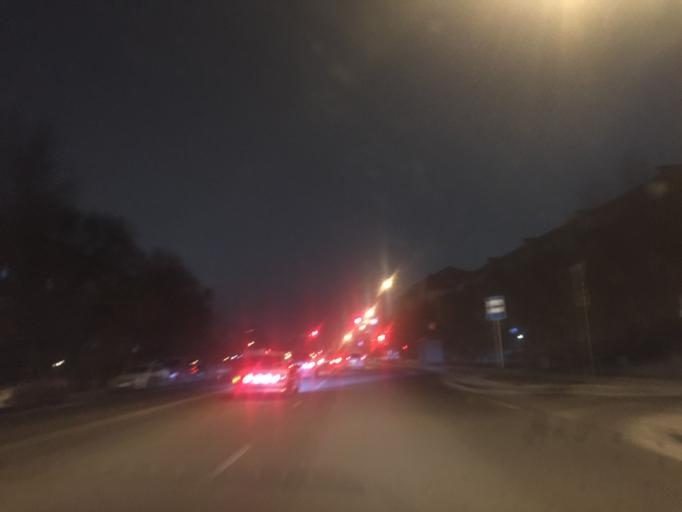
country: KZ
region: Astana Qalasy
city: Astana
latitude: 51.1884
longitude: 71.4210
